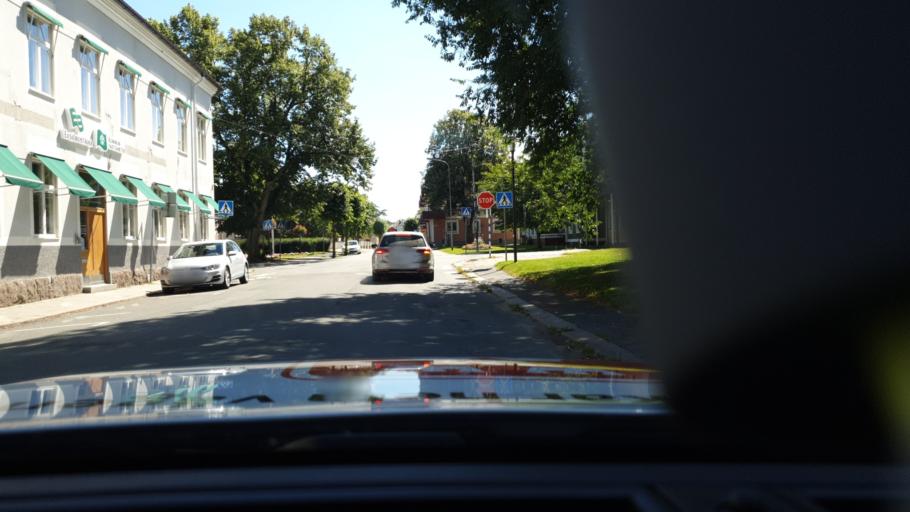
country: SE
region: Joenkoeping
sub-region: Eksjo Kommun
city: Eksjoe
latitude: 57.6675
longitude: 14.9727
